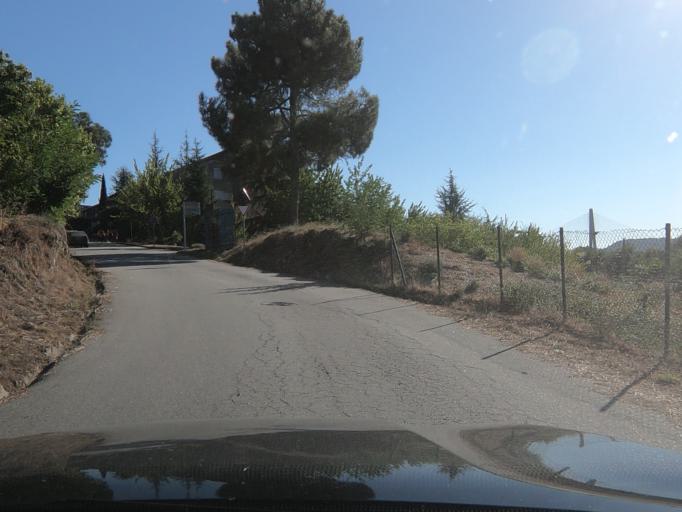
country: PT
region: Vila Real
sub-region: Vila Real
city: Vila Real
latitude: 41.2855
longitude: -7.7452
